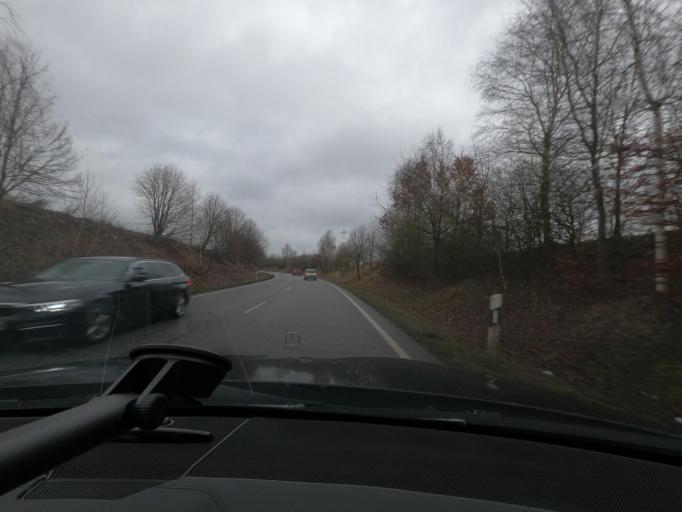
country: DE
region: Hesse
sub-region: Regierungsbezirk Kassel
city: Martinhagen
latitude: 51.2996
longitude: 9.2368
